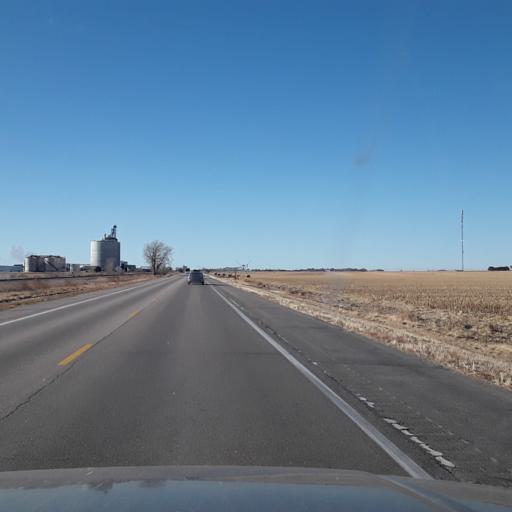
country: US
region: Nebraska
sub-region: Kearney County
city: Minden
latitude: 40.4867
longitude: -99.0656
